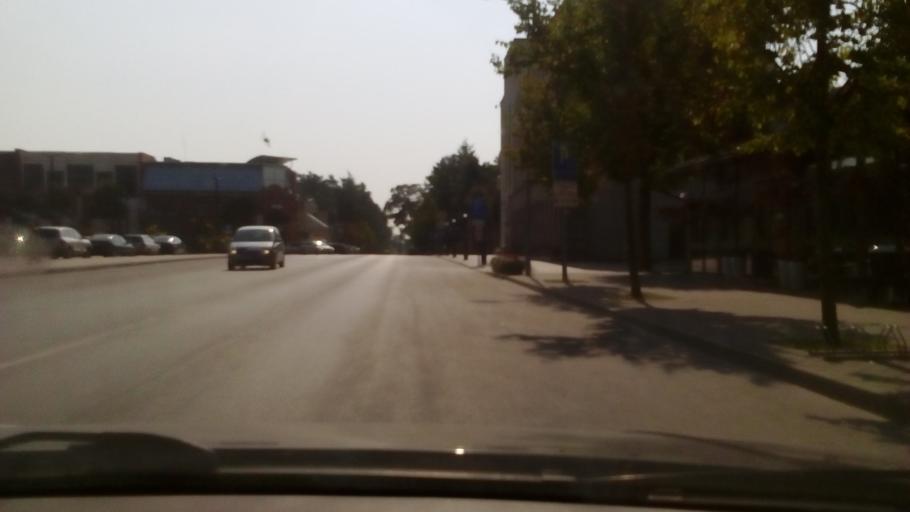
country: LT
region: Alytaus apskritis
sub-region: Alytus
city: Alytus
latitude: 54.3972
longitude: 24.0486
